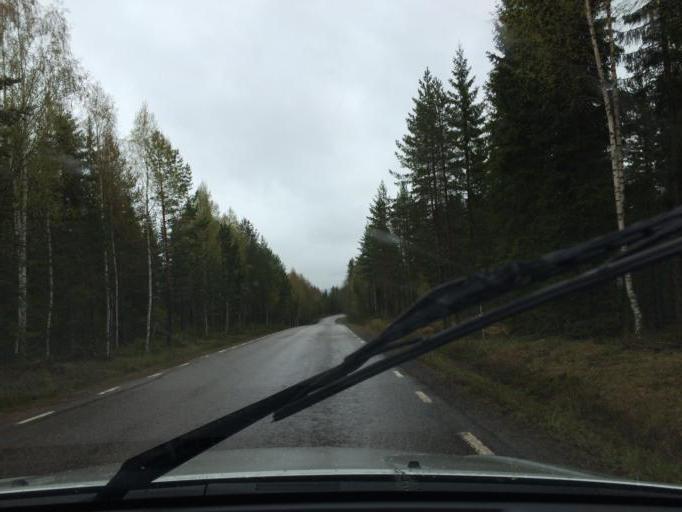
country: SE
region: Dalarna
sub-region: Ludvika Kommun
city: Abborrberget
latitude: 60.0636
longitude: 14.8485
